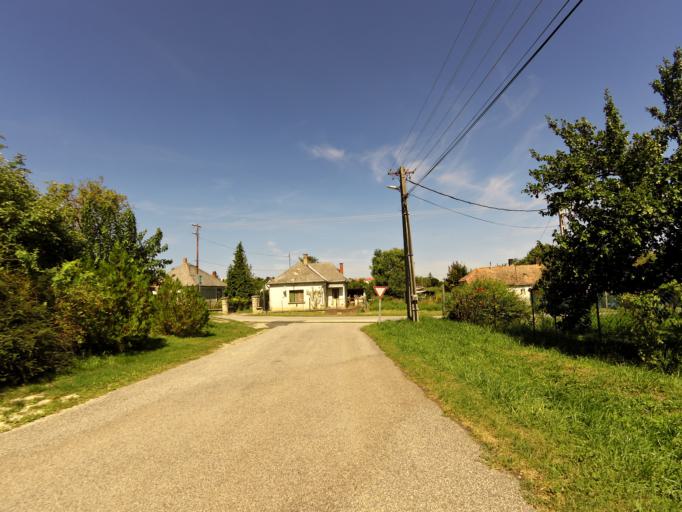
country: HU
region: Veszprem
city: Tapolca
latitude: 46.8242
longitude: 17.3726
